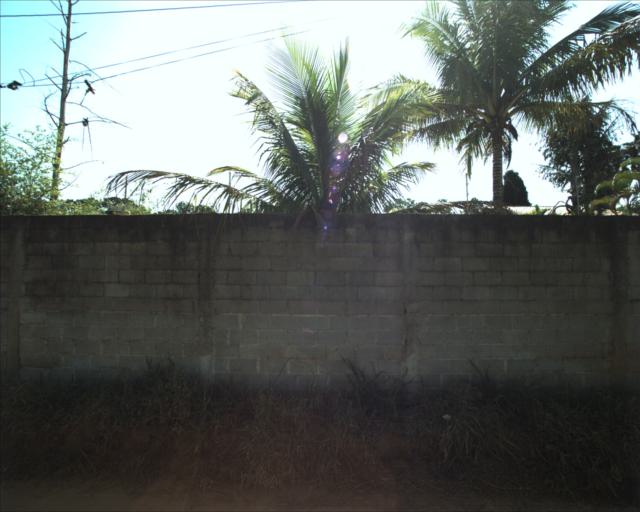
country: BR
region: Sao Paulo
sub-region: Aracoiaba Da Serra
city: Aracoiaba da Serra
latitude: -23.4833
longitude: -47.5390
